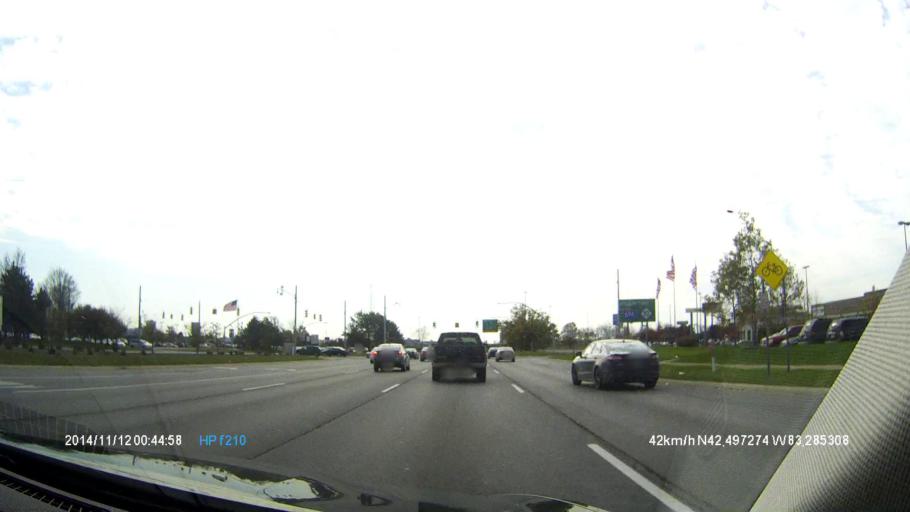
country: US
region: Michigan
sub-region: Oakland County
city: Bingham Farms
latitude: 42.4976
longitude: -83.2853
